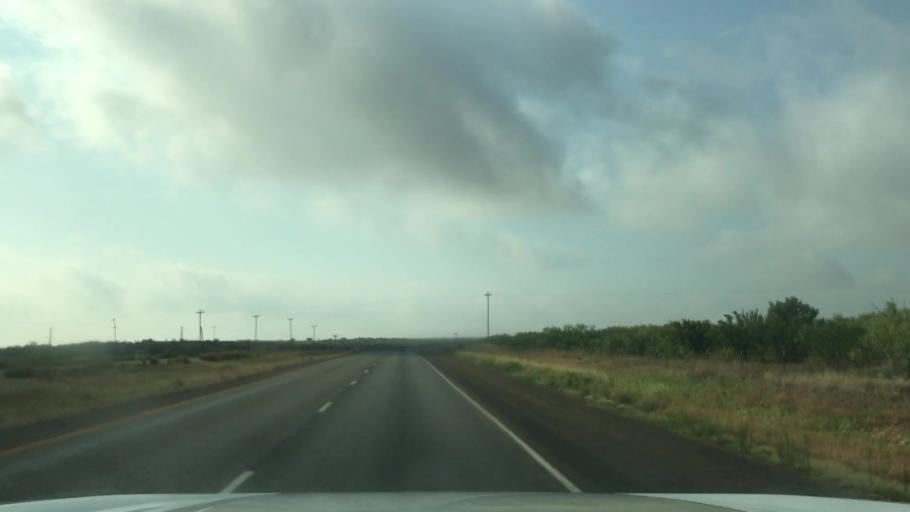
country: US
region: Texas
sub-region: Garza County
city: Post
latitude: 33.1638
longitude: -101.3494
